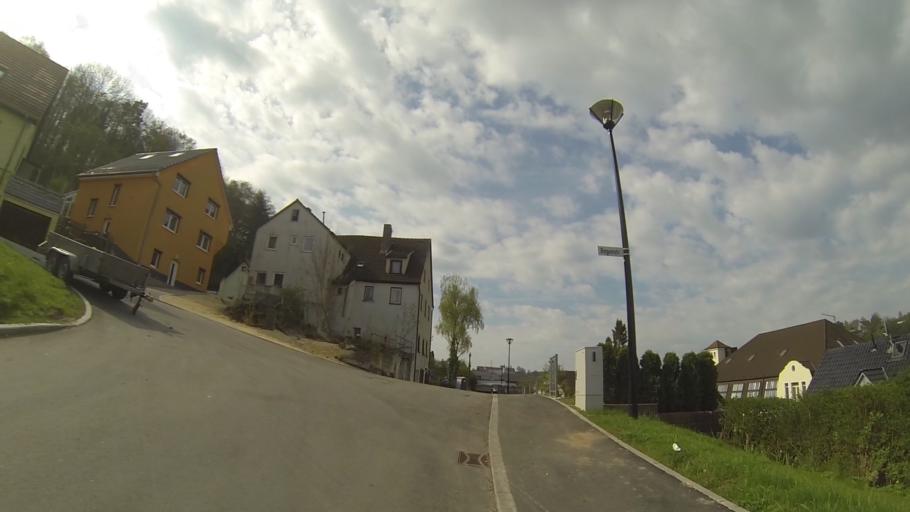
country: DE
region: Baden-Wuerttemberg
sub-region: Regierungsbezirk Stuttgart
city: Heidenheim an der Brenz
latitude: 48.6851
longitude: 10.1586
